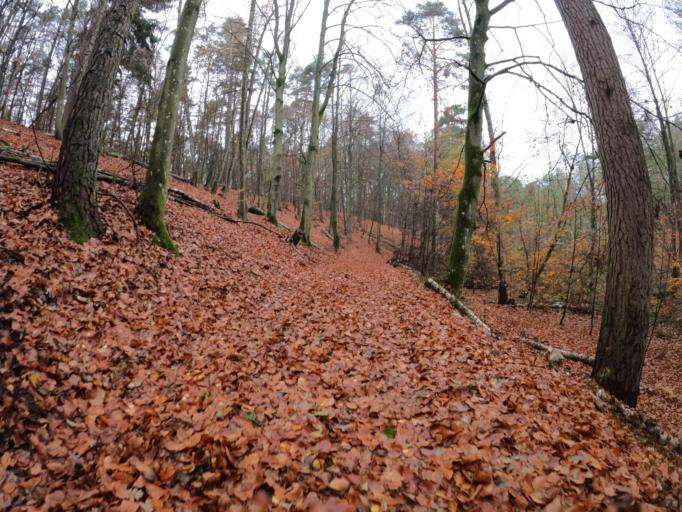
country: PL
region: West Pomeranian Voivodeship
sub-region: Powiat walecki
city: Tuczno
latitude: 53.2702
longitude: 16.2517
